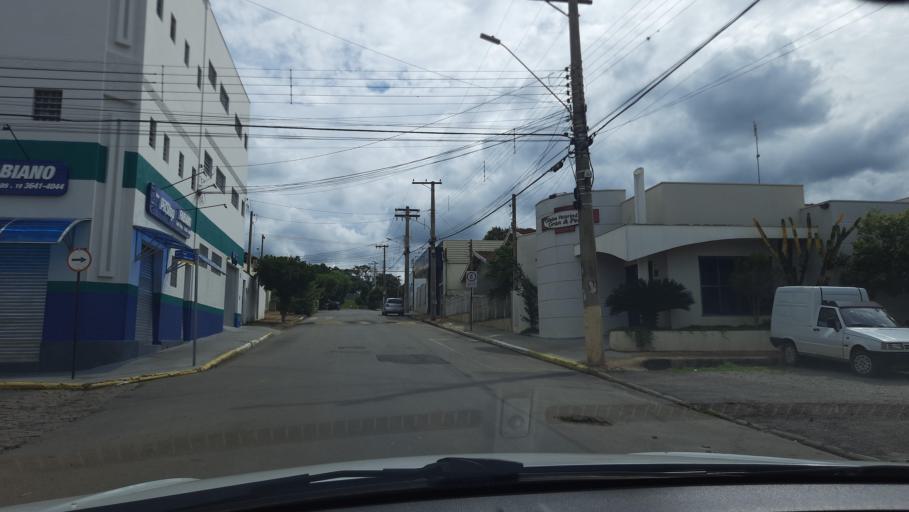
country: BR
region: Sao Paulo
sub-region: Vargem Grande Do Sul
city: Vargem Grande do Sul
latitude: -21.8403
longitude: -46.9012
